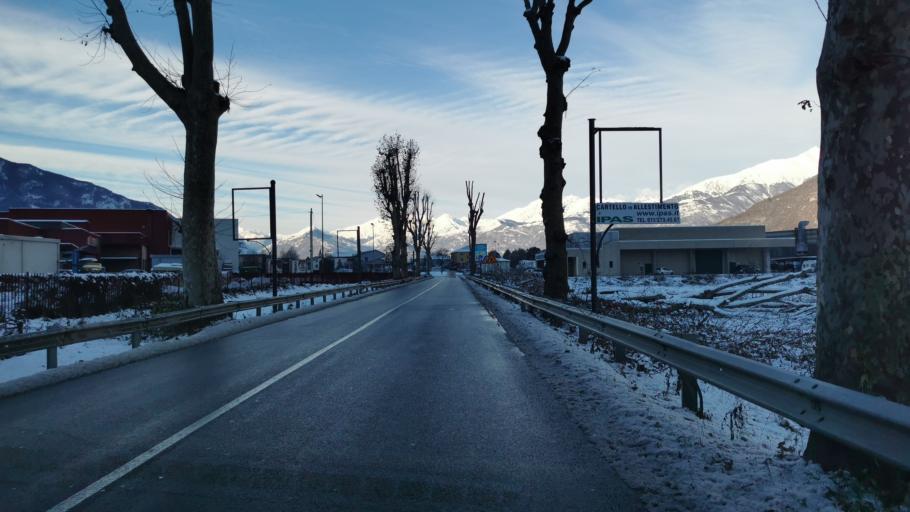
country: IT
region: Lombardy
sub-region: Provincia di Sondrio
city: Rogolo
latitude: 46.1367
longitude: 9.4804
